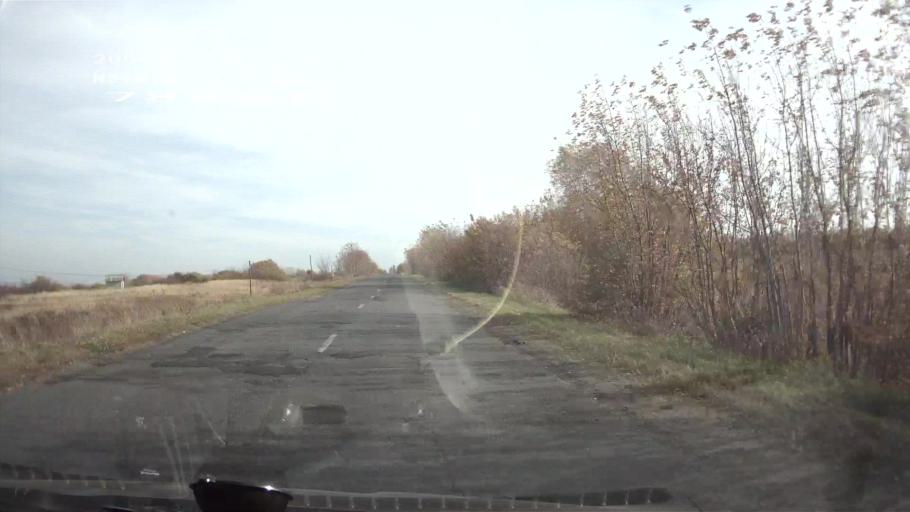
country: RU
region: Chuvashia
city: Alatyr'
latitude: 54.8450
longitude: 46.4624
